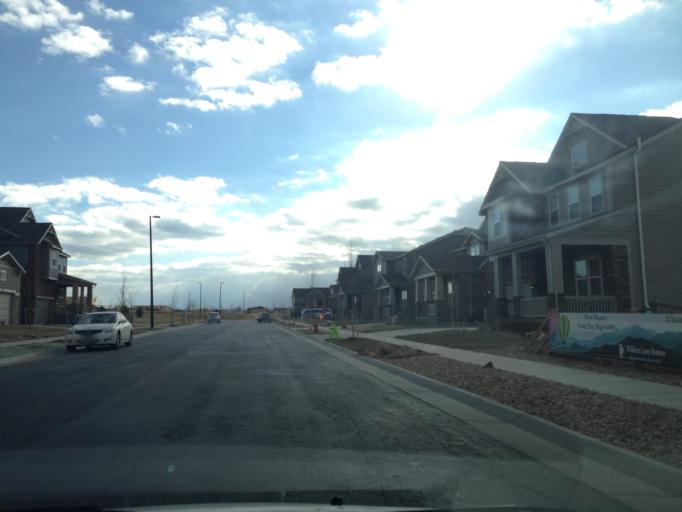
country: US
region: Colorado
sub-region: Boulder County
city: Lafayette
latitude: 40.0315
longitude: -105.0868
